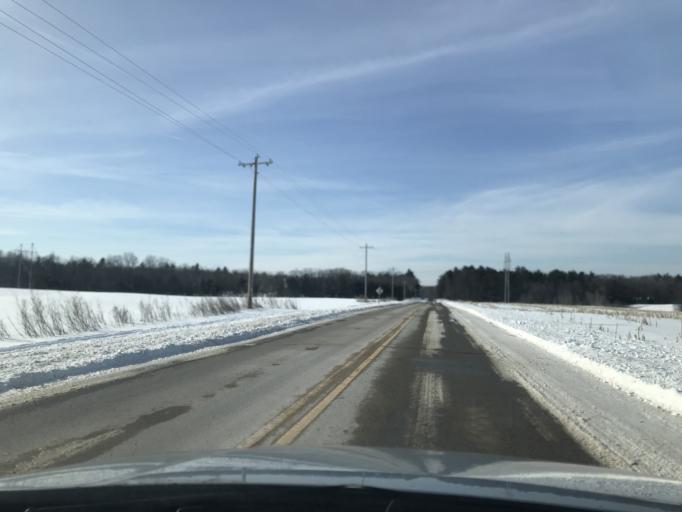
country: US
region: Wisconsin
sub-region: Oconto County
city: Oconto Falls
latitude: 45.1475
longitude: -88.1784
